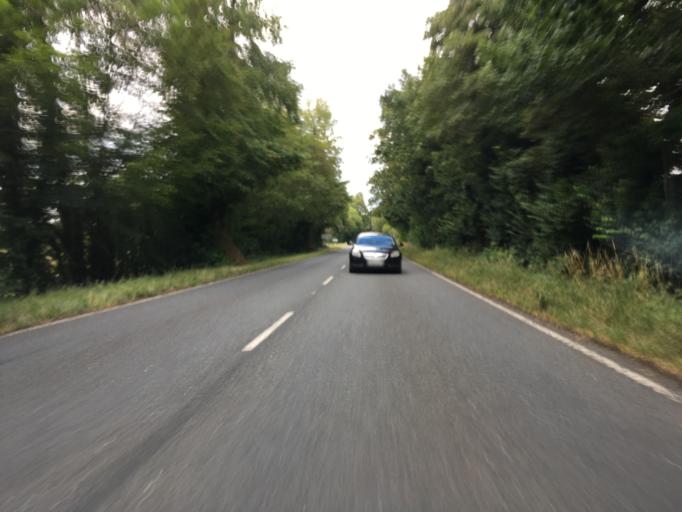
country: GB
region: England
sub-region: Hampshire
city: Kings Worthy
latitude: 51.1349
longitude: -1.2565
